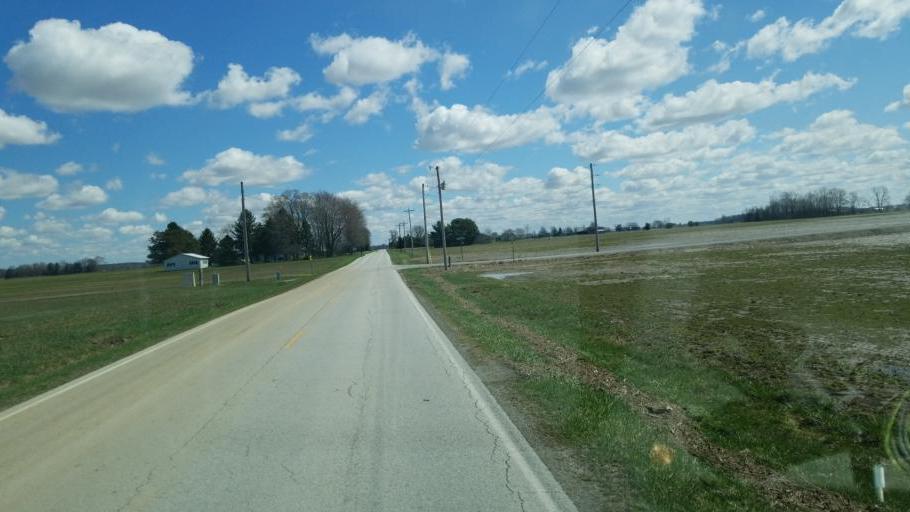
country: US
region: Ohio
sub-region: Hancock County
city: Findlay
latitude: 41.0368
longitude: -83.5115
